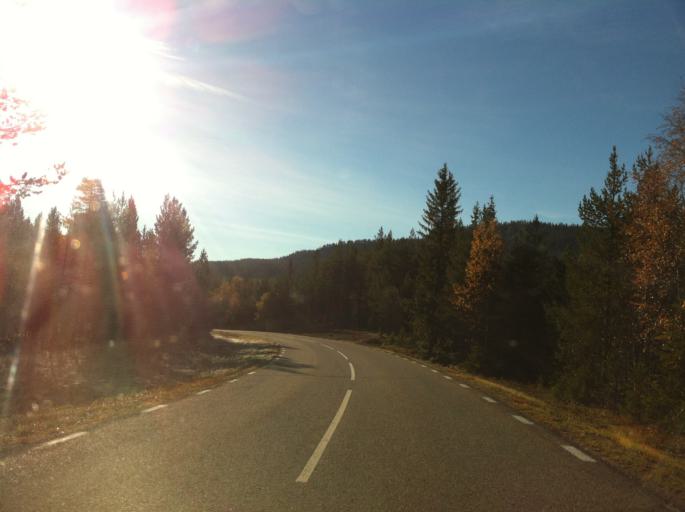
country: NO
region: Hedmark
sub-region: Engerdal
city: Engerdal
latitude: 61.9979
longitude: 12.4579
